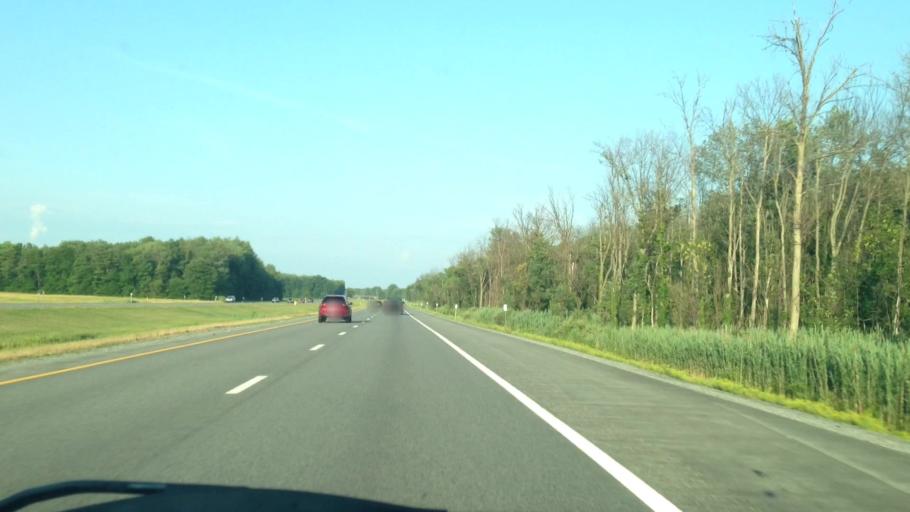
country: US
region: New York
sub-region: Madison County
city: Bolivar
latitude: 43.0911
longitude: -75.9225
